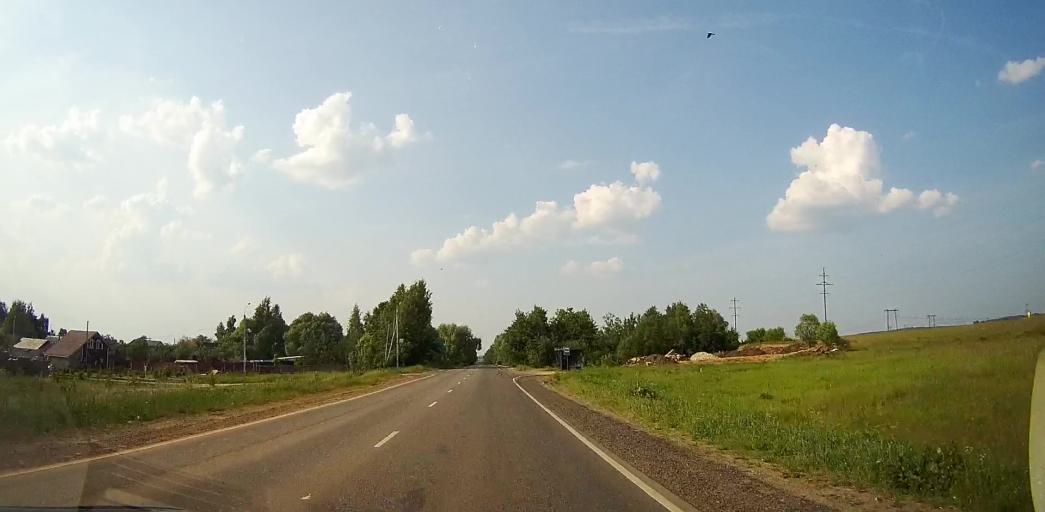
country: RU
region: Moskovskaya
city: Ostrovtsy
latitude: 55.5238
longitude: 38.0027
